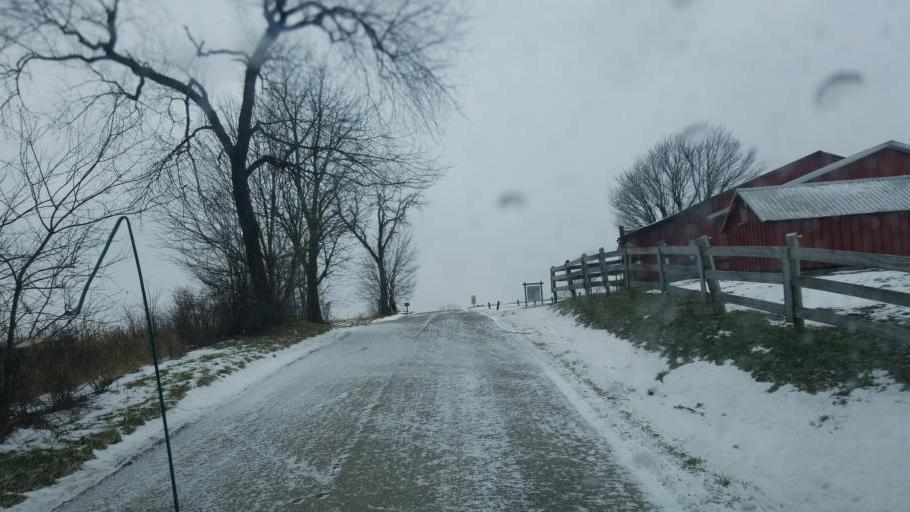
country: US
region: Ohio
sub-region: Wayne County
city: Apple Creek
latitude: 40.6824
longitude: -81.8304
